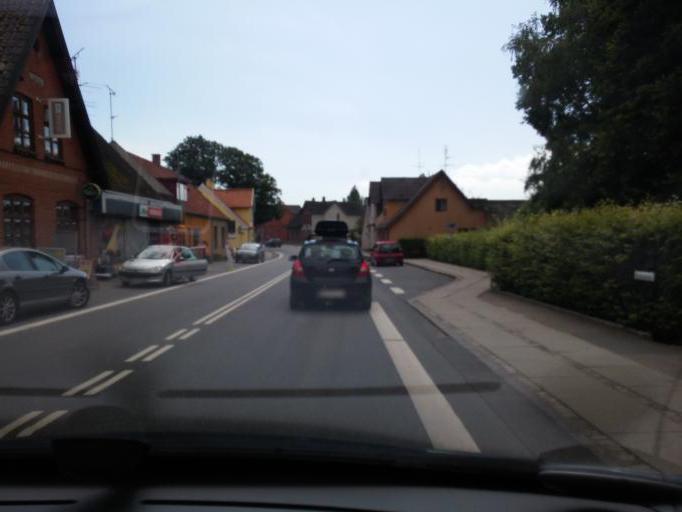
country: DK
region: South Denmark
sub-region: Langeland Kommune
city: Rudkobing
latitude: 54.8643
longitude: 10.7298
